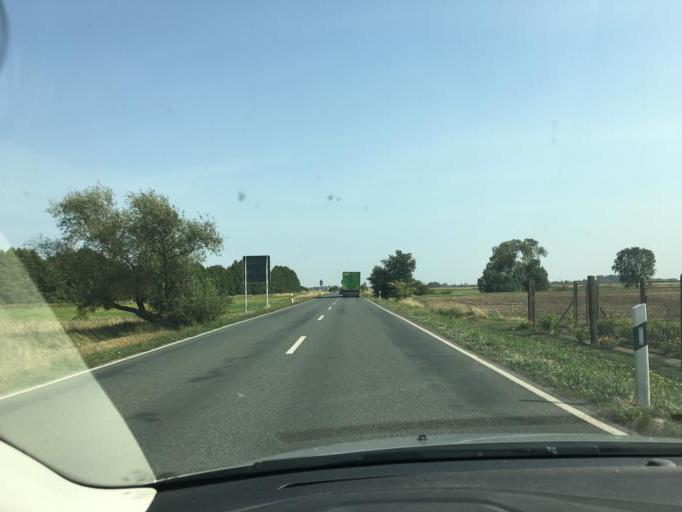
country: DE
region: Saxony-Anhalt
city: Plotzky
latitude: 52.0058
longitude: 11.8014
